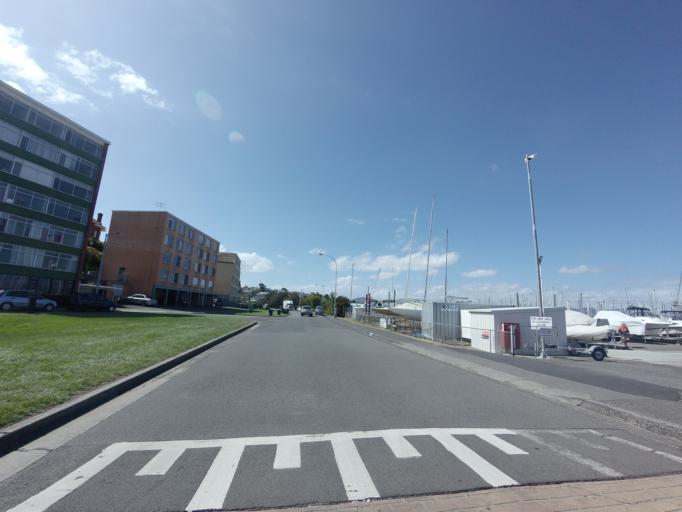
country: AU
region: Tasmania
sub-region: Hobart
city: Sandy Bay
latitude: -42.8979
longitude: 147.3319
